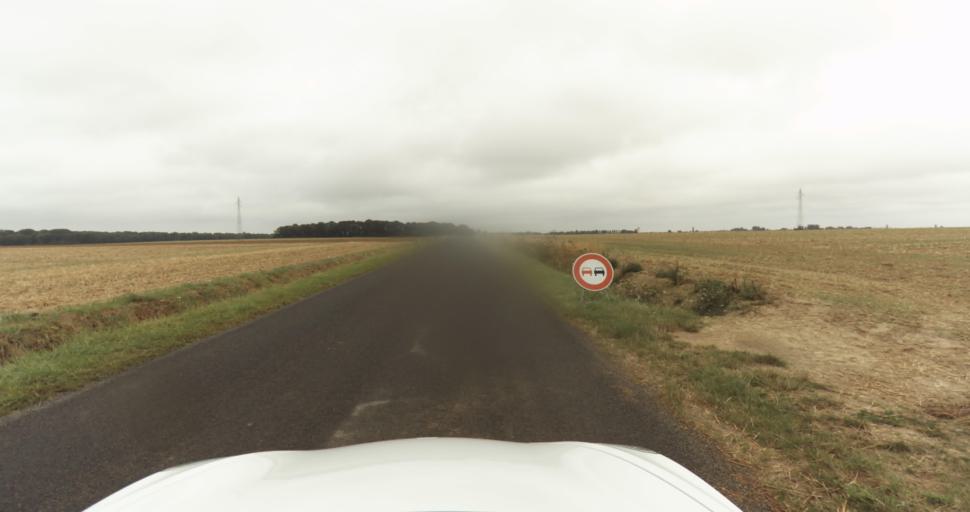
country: FR
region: Haute-Normandie
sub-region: Departement de l'Eure
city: Claville
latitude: 49.0905
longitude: 1.0548
